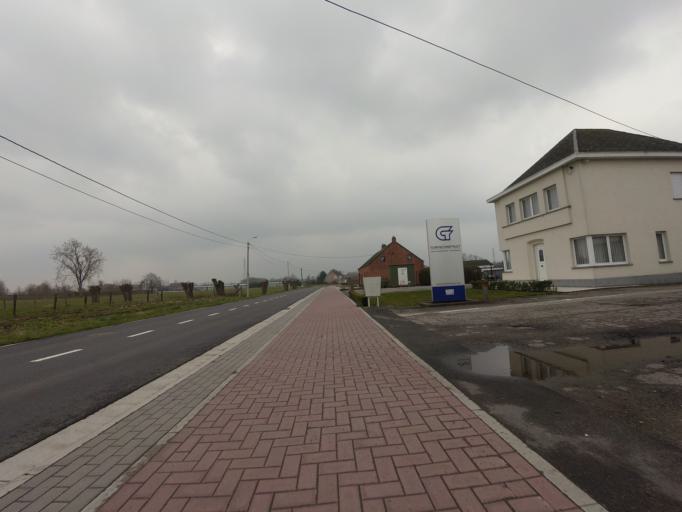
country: BE
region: Flanders
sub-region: Provincie Antwerpen
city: Putte
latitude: 51.0550
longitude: 4.5973
